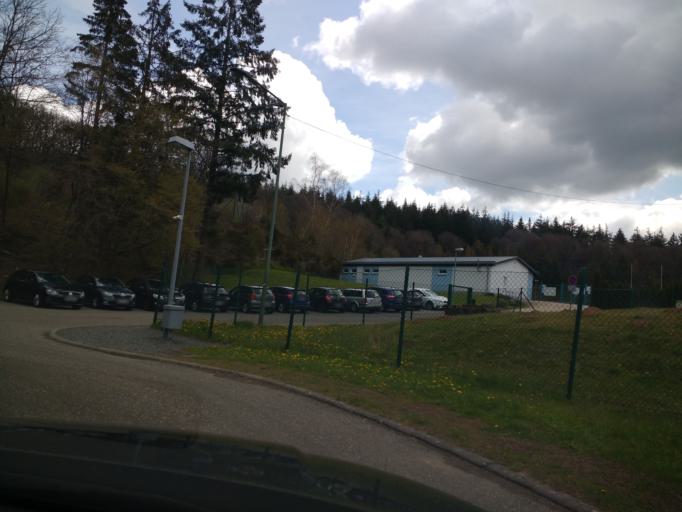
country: DE
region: Rheinland-Pfalz
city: Junkerath
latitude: 50.3482
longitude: 6.5809
